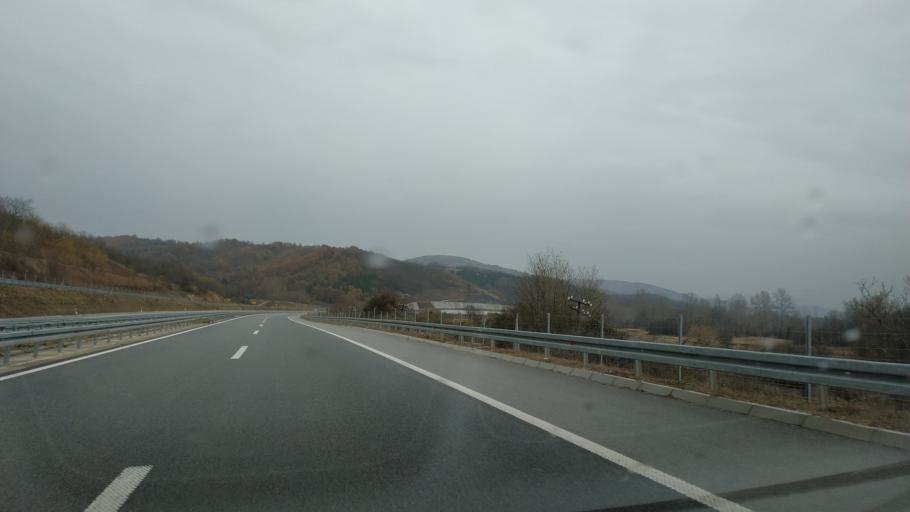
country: RS
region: Central Serbia
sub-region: Pirotski Okrug
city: Bela Palanka
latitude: 43.2314
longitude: 22.4454
